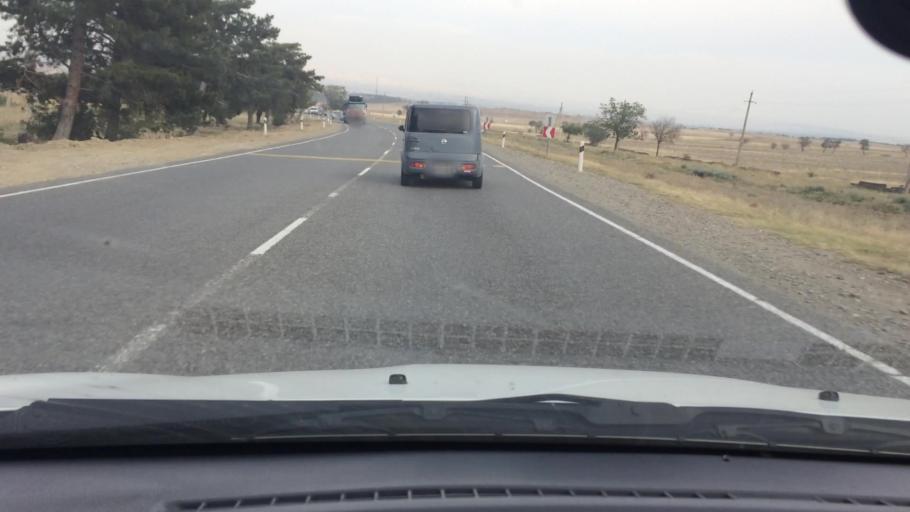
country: GE
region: T'bilisi
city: Tbilisi
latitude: 41.6386
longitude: 44.8738
